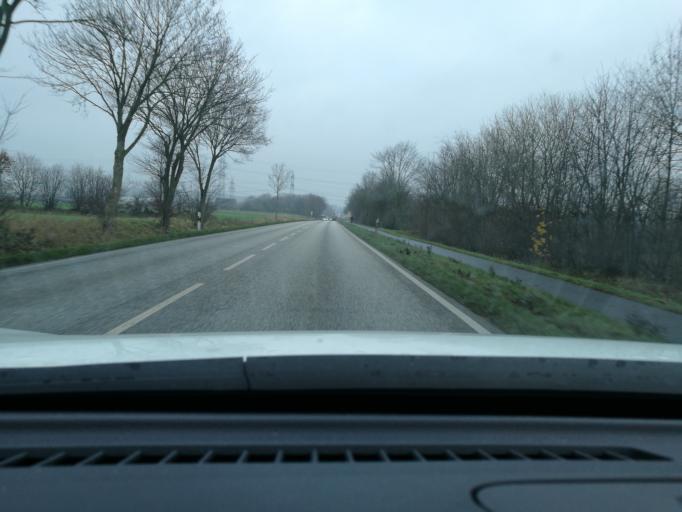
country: DE
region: Schleswig-Holstein
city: Borgstedt
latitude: 54.3384
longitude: 9.6974
